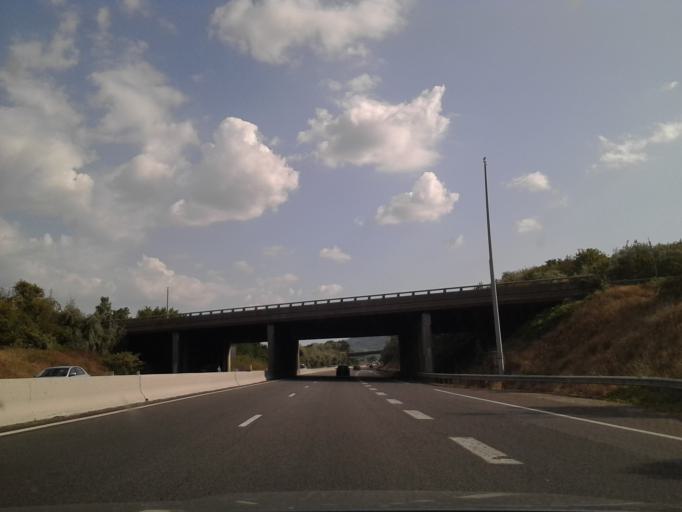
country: FR
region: Auvergne
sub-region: Departement du Puy-de-Dome
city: Aulnat
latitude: 45.7754
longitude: 3.1405
